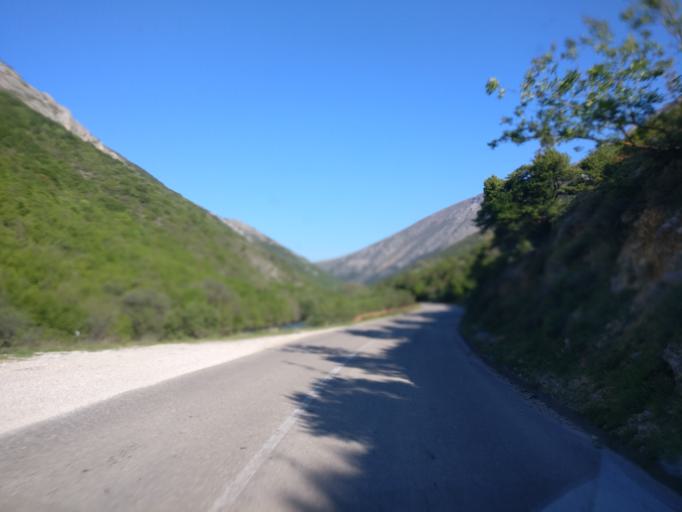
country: BA
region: Federation of Bosnia and Herzegovina
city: Stolac
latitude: 43.0802
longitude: 18.0133
